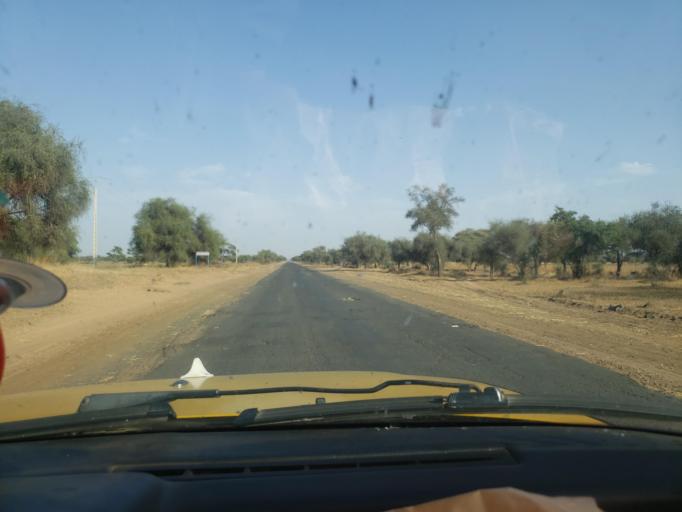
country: SN
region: Louga
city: Louga
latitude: 15.5073
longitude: -15.9684
